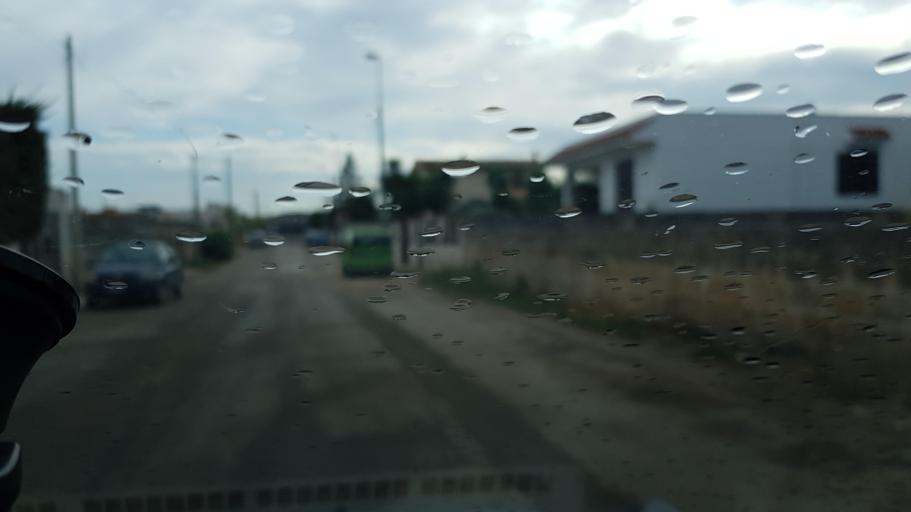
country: IT
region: Apulia
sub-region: Provincia di Brindisi
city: Torre Santa Susanna
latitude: 40.4691
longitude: 17.7312
